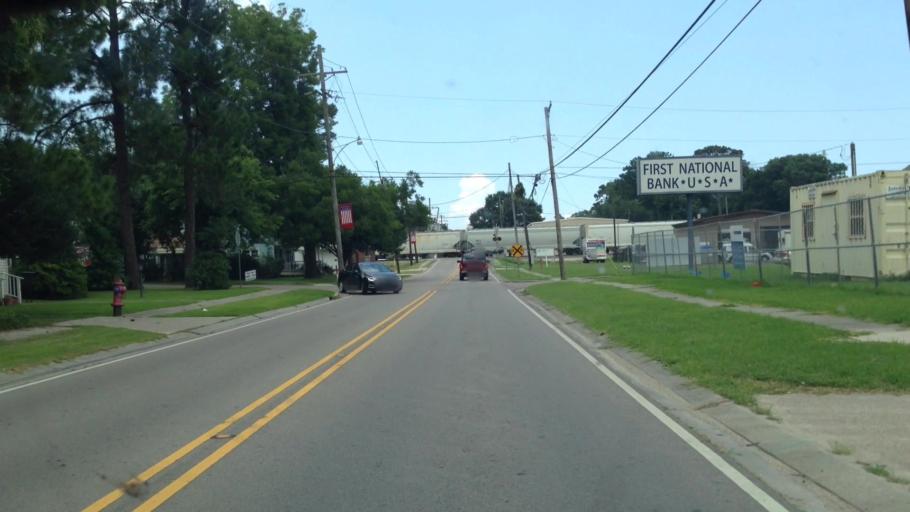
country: US
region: Louisiana
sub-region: Saint Charles Parish
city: Norco
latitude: 30.0098
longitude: -90.4090
